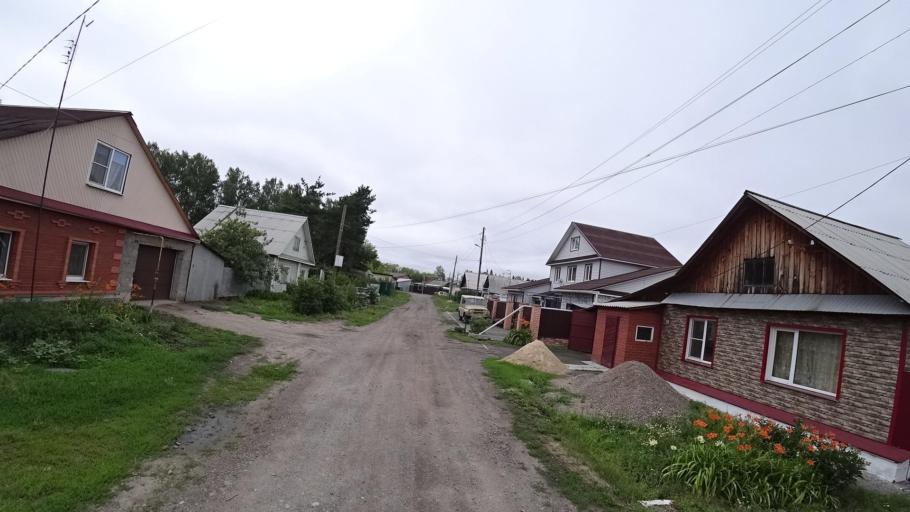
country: RU
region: Sverdlovsk
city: Kamyshlov
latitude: 56.8476
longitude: 62.7606
